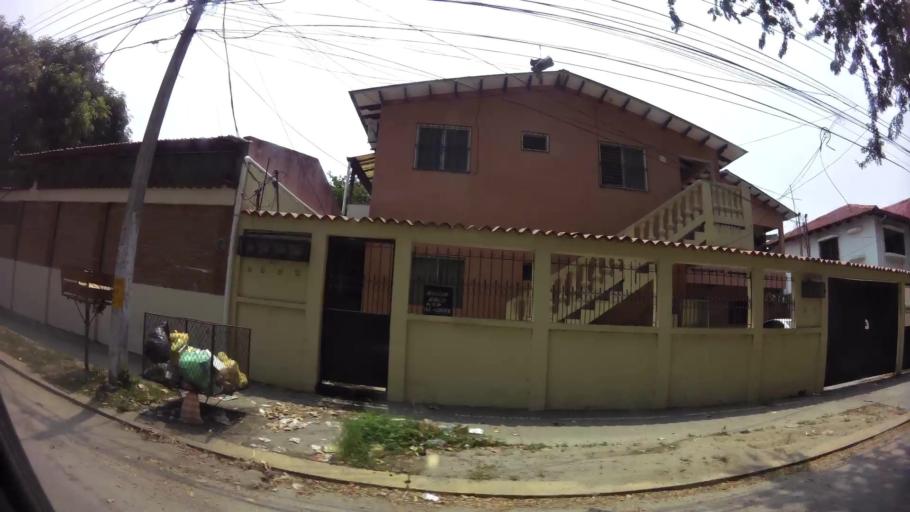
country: HN
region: Cortes
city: San Pedro Sula
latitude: 15.4908
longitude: -88.0004
